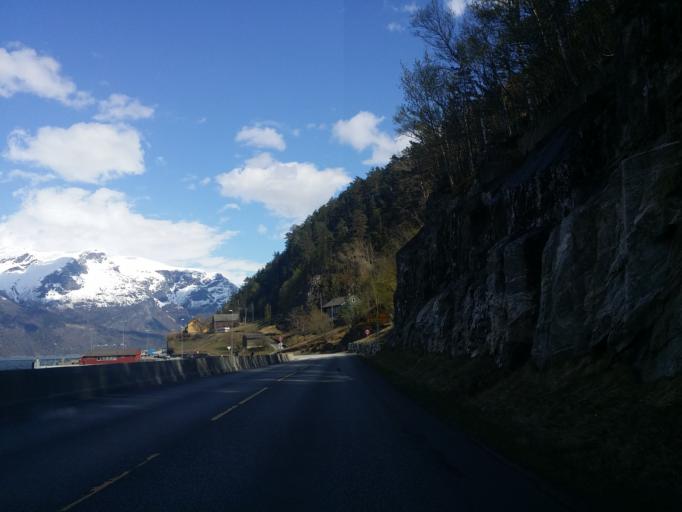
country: NO
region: Hordaland
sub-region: Ulvik
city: Ulvik
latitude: 60.4702
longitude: 6.9043
